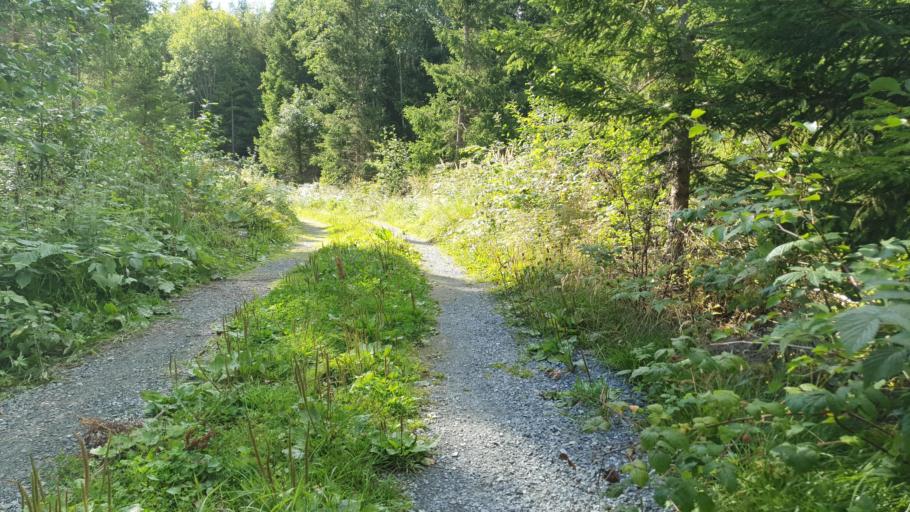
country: NO
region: Nord-Trondelag
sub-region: Levanger
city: Levanger
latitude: 63.7722
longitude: 11.3691
